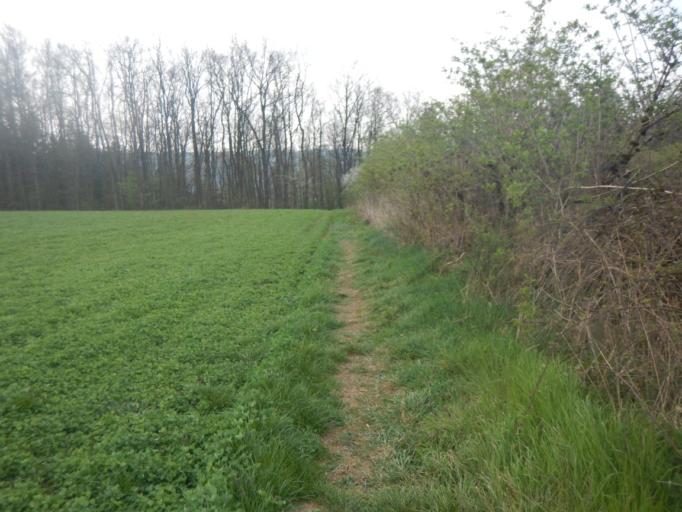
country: LU
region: Diekirch
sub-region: Canton de Wiltz
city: Esch-sur-Sure
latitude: 49.9159
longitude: 5.9398
